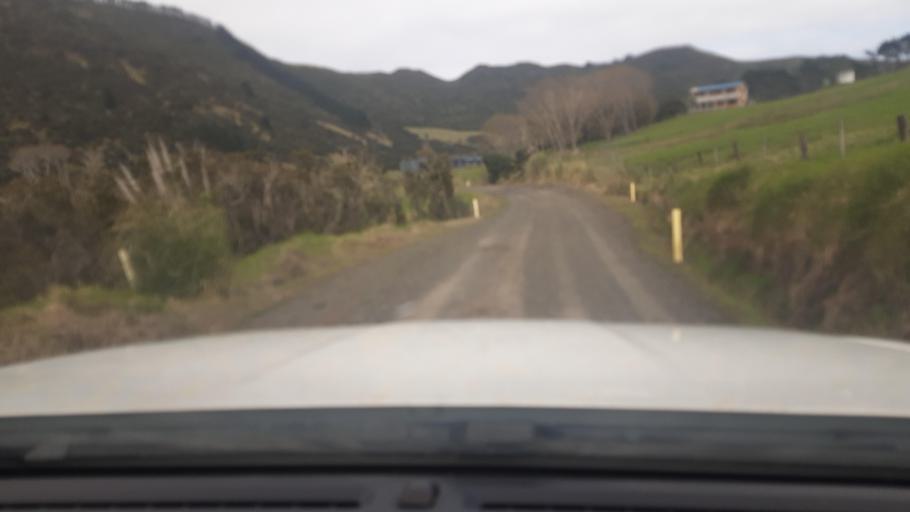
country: NZ
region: Northland
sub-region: Far North District
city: Ahipara
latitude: -35.3336
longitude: 173.2217
